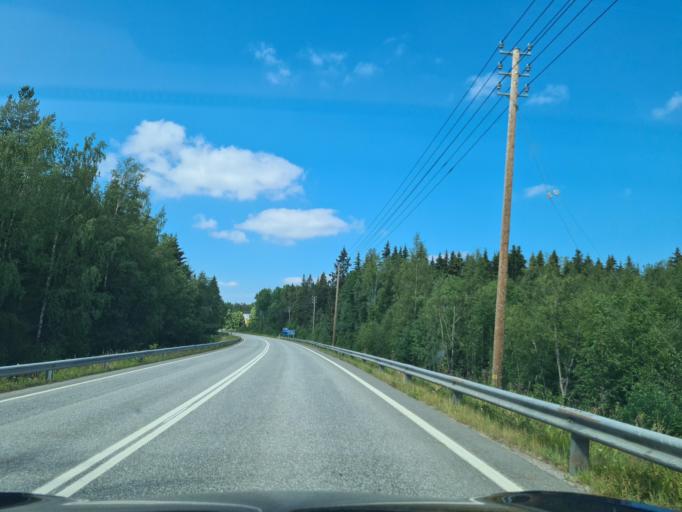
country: FI
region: Ostrobothnia
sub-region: Vaasa
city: Vaasa
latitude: 63.1898
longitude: 21.5644
